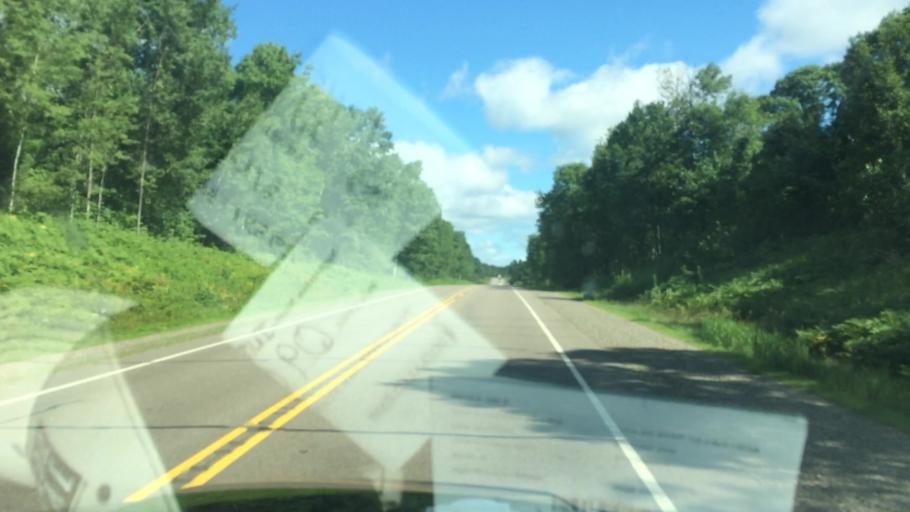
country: US
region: Wisconsin
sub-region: Oneida County
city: Rhinelander
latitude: 45.5798
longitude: -89.5693
